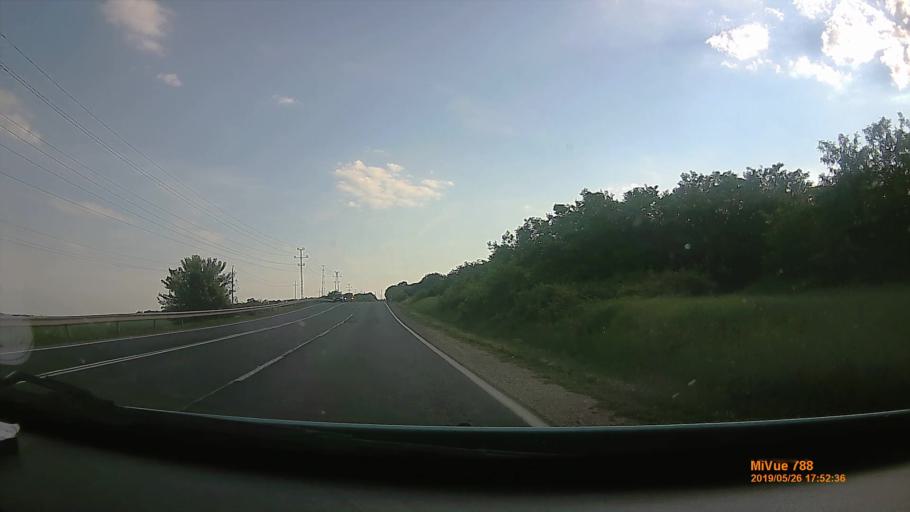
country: HU
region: Borsod-Abauj-Zemplen
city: Szikszo
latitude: 48.1627
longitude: 20.9049
